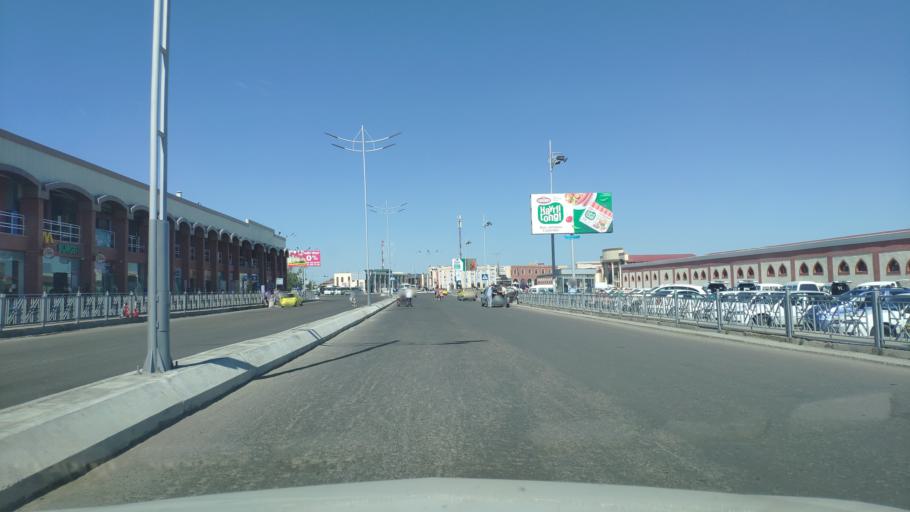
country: UZ
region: Bukhara
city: Bukhara
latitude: 39.7806
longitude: 64.4011
